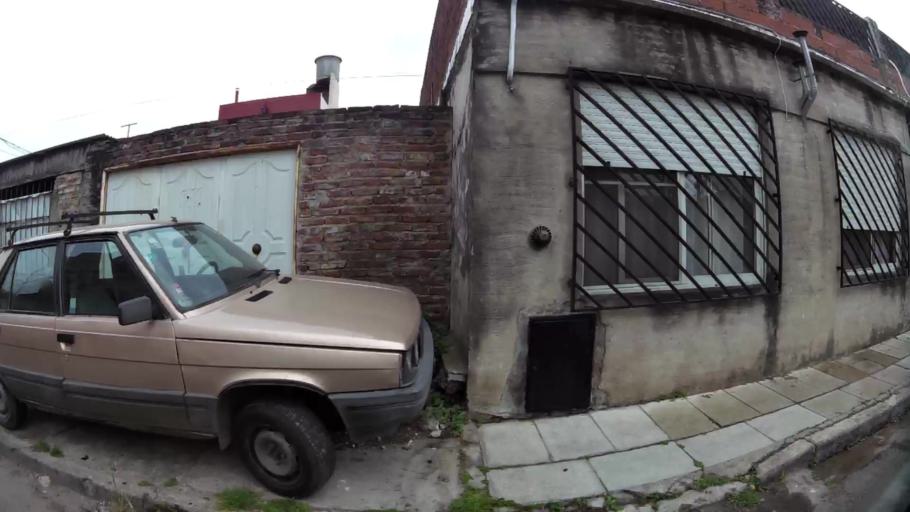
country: AR
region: Buenos Aires F.D.
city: Villa Lugano
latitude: -34.6850
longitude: -58.5109
